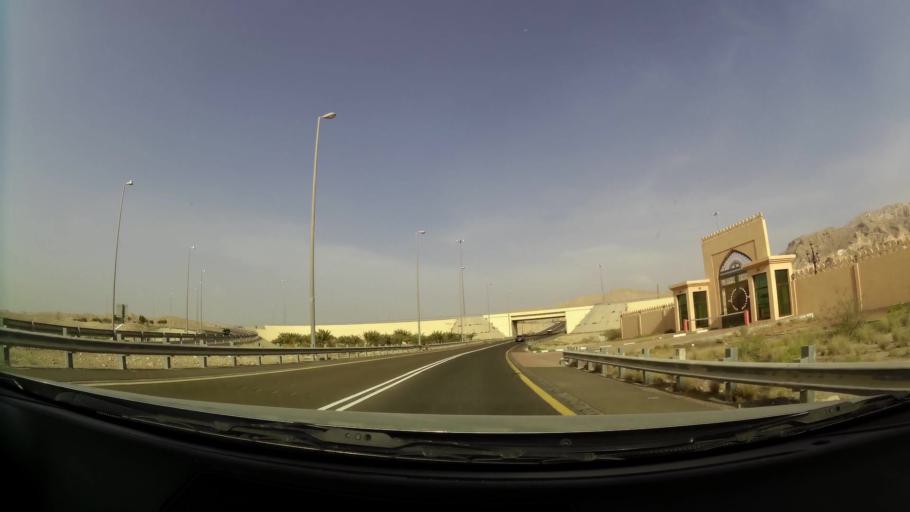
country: AE
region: Abu Dhabi
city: Al Ain
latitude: 24.1130
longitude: 55.7519
